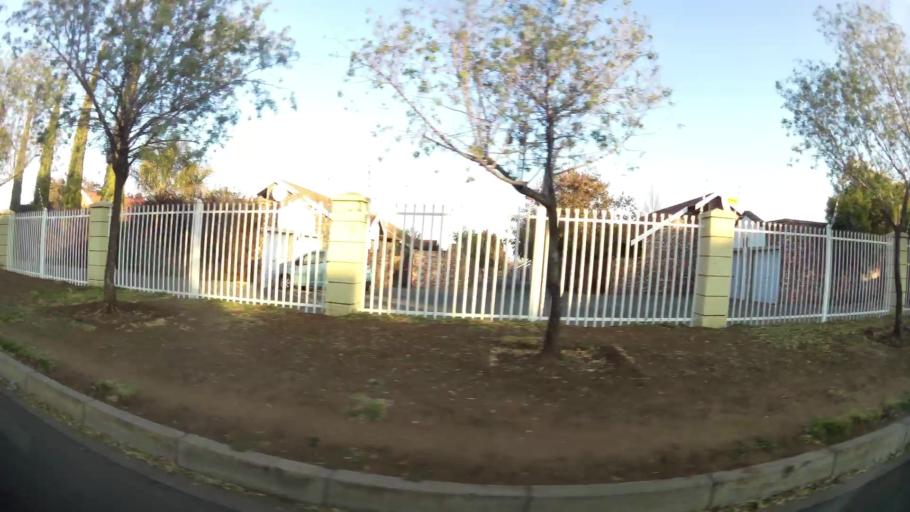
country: ZA
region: Orange Free State
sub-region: Mangaung Metropolitan Municipality
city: Bloemfontein
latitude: -29.0931
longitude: 26.1671
